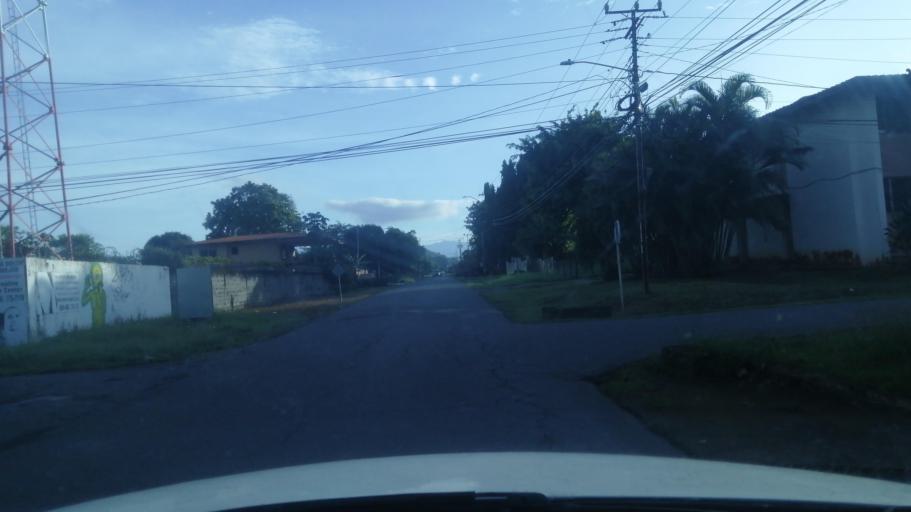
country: PA
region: Chiriqui
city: Mata del Nance
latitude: 8.4477
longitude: -82.4208
